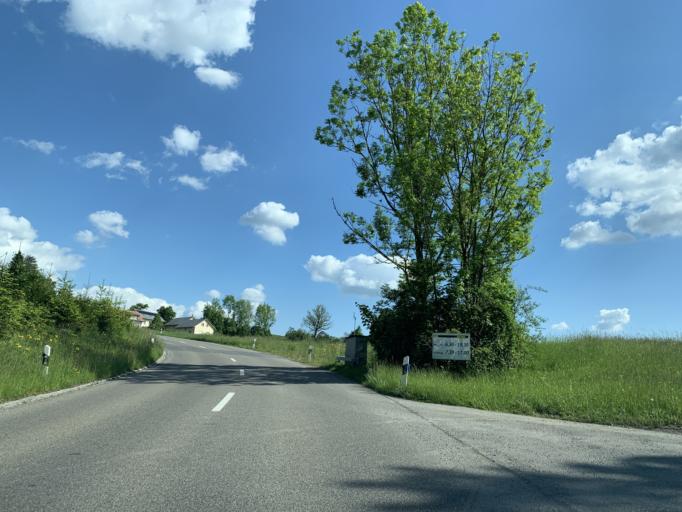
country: CH
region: Zurich
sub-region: Bezirk Pfaeffikon
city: Effretikon / Watt
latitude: 47.4370
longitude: 8.7131
